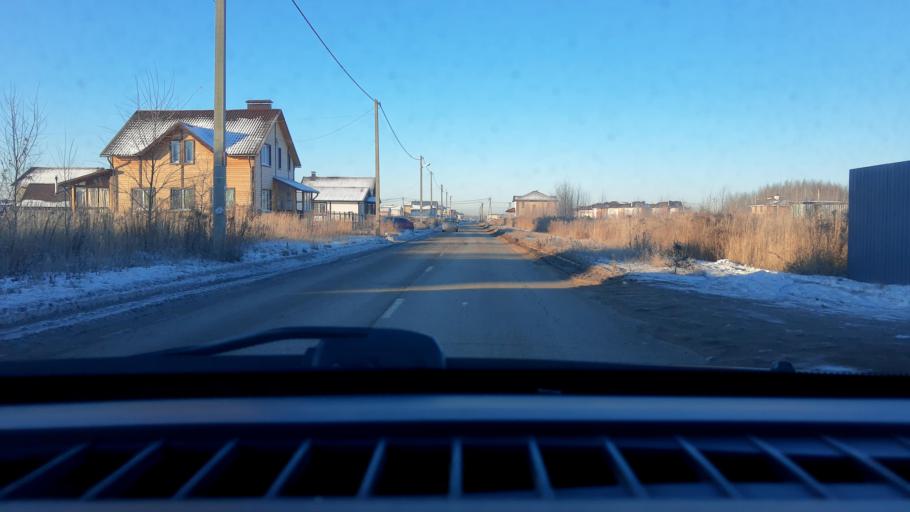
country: RU
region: Nizjnij Novgorod
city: Bor
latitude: 56.3899
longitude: 44.0685
